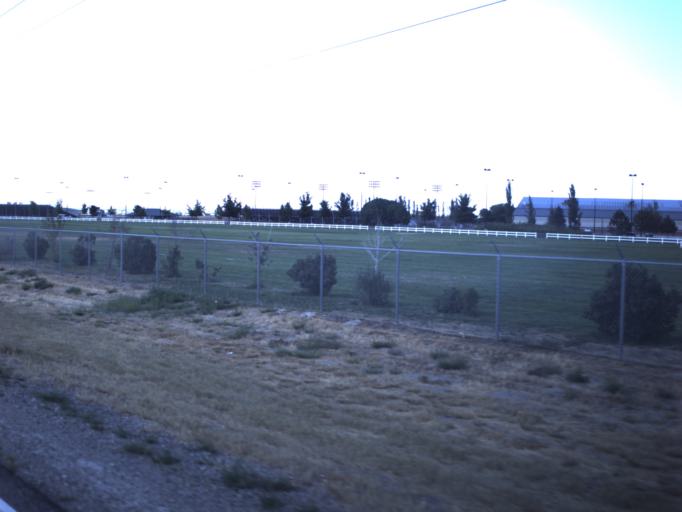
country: US
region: Utah
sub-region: Tooele County
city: Erda
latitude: 40.5687
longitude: -112.3714
